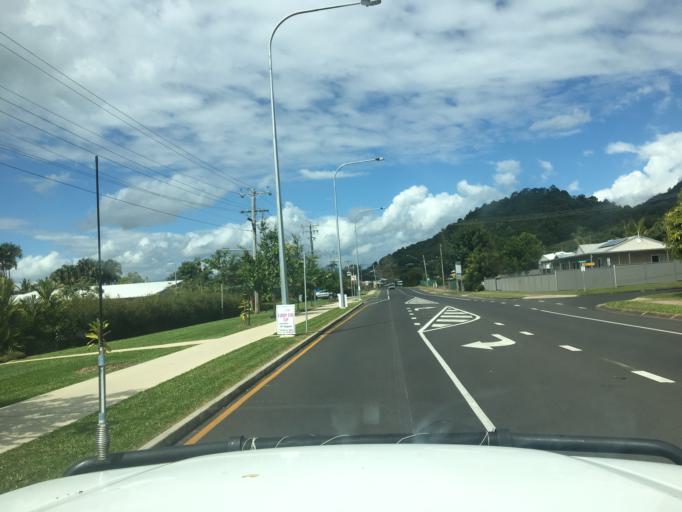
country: AU
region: Queensland
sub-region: Cairns
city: Woree
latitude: -16.9627
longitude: 145.7401
